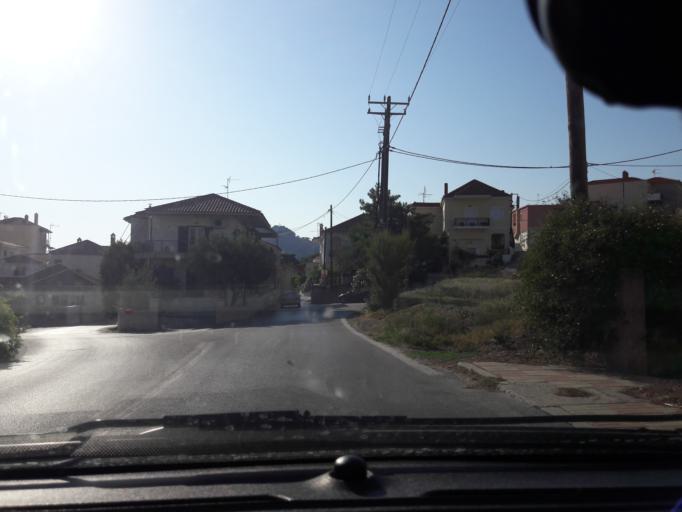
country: GR
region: North Aegean
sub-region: Nomos Lesvou
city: Myrina
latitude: 39.8719
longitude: 25.0667
